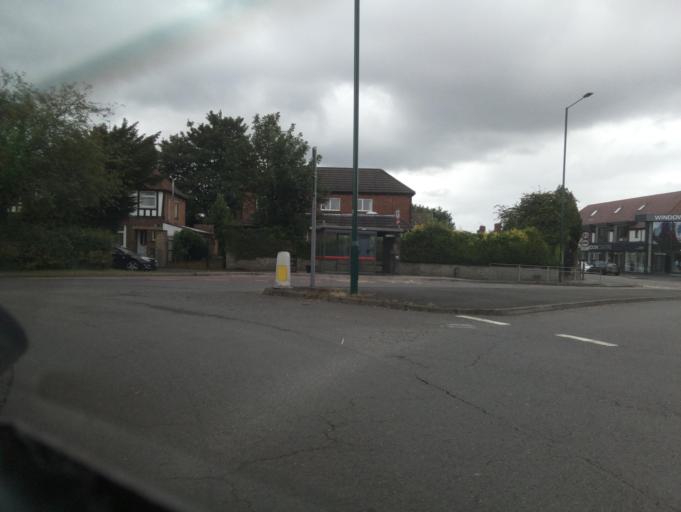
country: GB
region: England
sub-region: Solihull
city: Shirley
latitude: 52.4007
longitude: -1.8147
